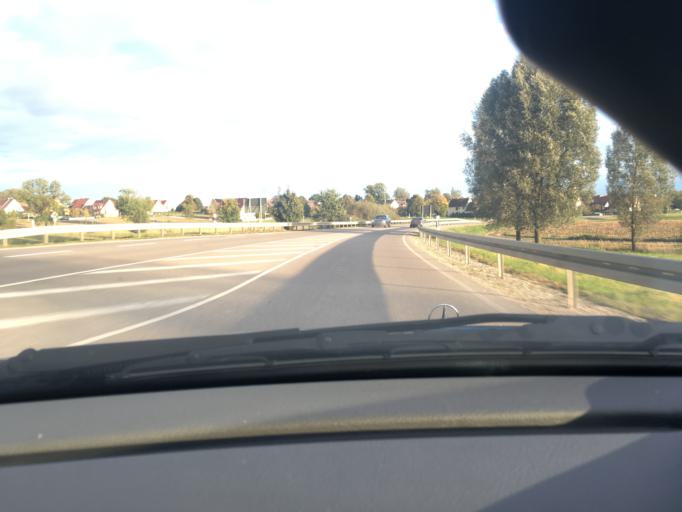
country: DE
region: Bavaria
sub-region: Swabia
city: Gablingen
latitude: 48.4291
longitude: 10.8252
